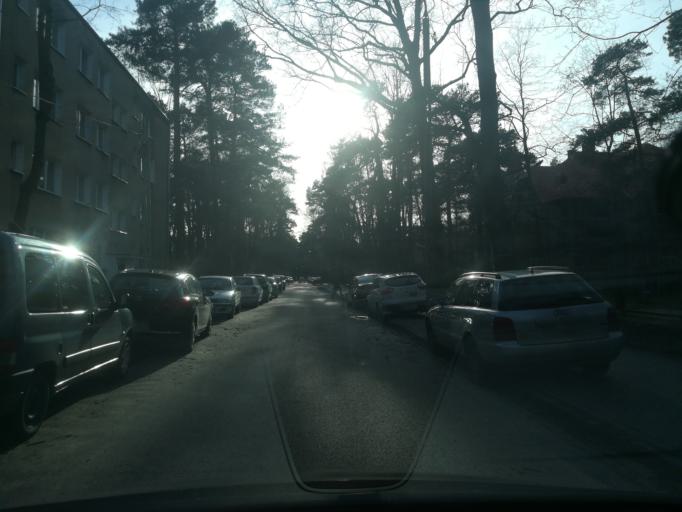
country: PL
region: Masovian Voivodeship
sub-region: Powiat piaseczynski
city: Konstancin-Jeziorna
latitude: 52.0862
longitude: 21.1247
